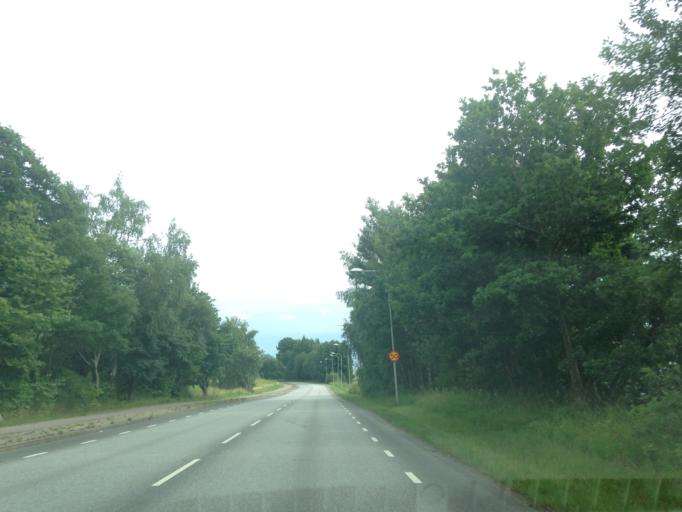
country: SE
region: Vaestra Goetaland
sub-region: Goteborg
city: Goeteborg
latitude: 57.7432
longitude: 11.9529
